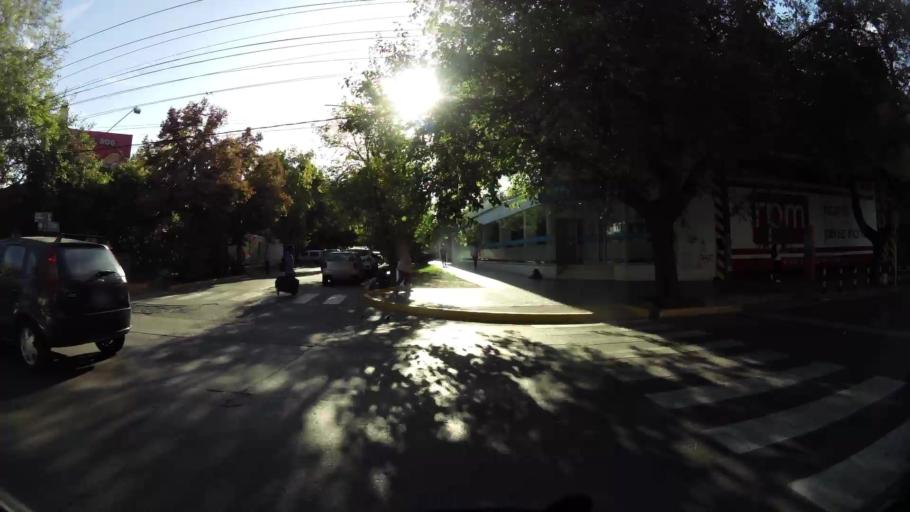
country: AR
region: Mendoza
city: Mendoza
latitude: -32.9047
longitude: -68.8431
